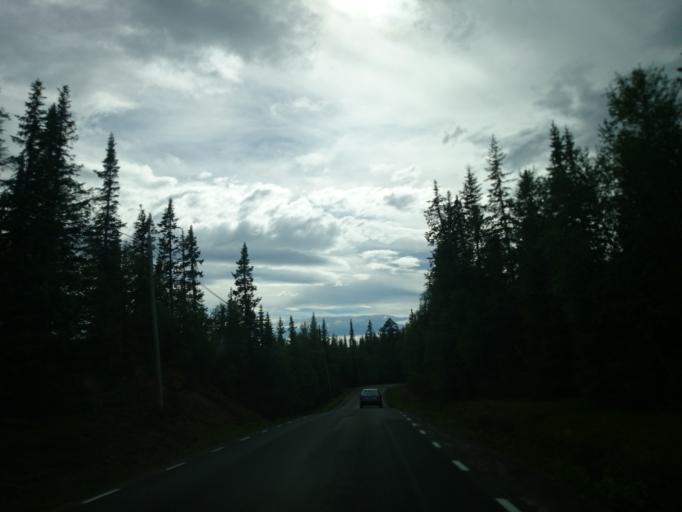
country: SE
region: Jaemtland
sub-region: Are Kommun
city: Are
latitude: 63.1577
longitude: 13.0404
